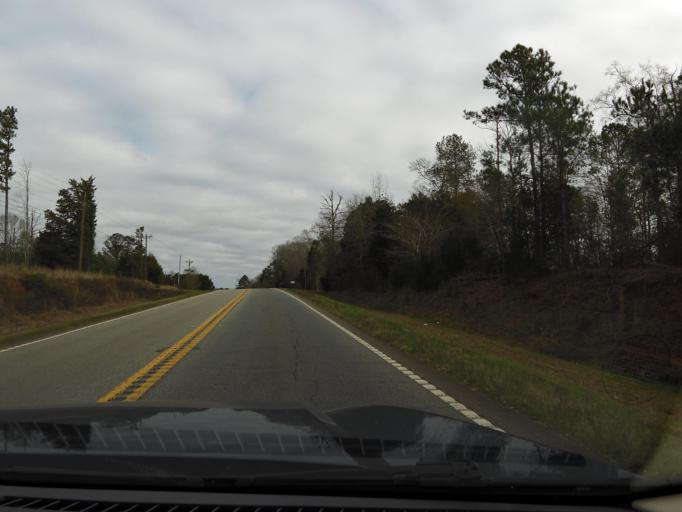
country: US
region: Georgia
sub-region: Quitman County
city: Georgetown
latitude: 31.8567
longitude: -85.0587
